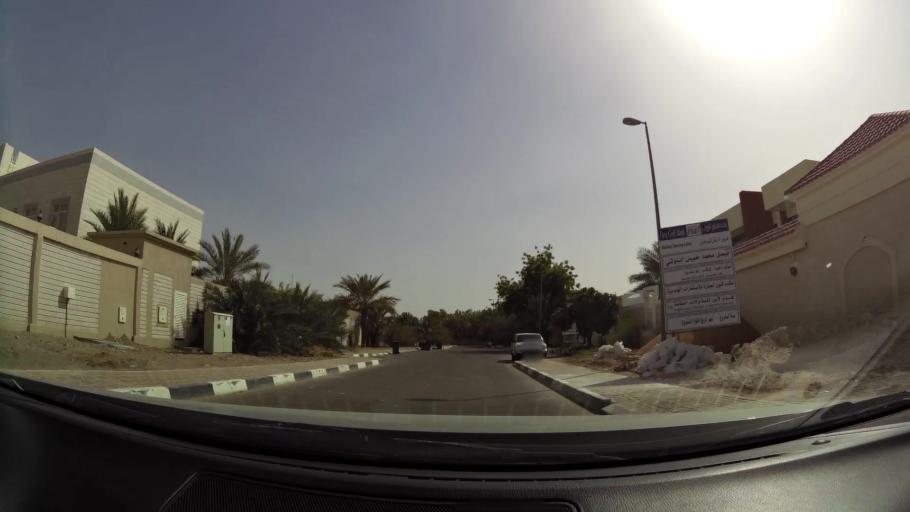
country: AE
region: Abu Dhabi
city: Al Ain
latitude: 24.2465
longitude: 55.6903
